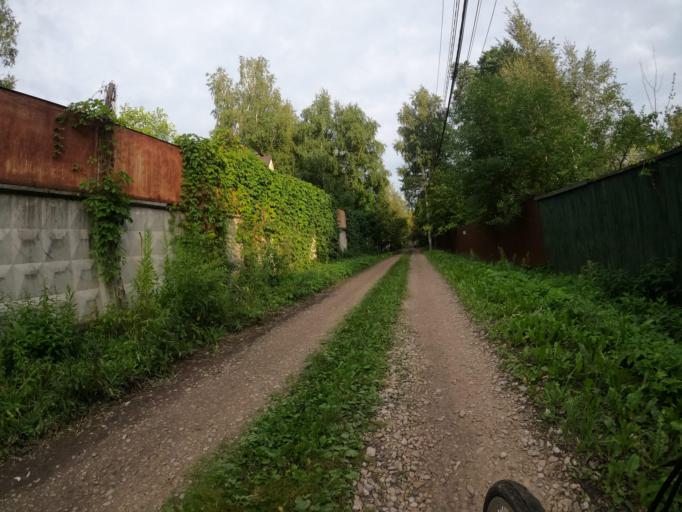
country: RU
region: Moskovskaya
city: Il'inskiy
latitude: 55.6425
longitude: 38.1121
